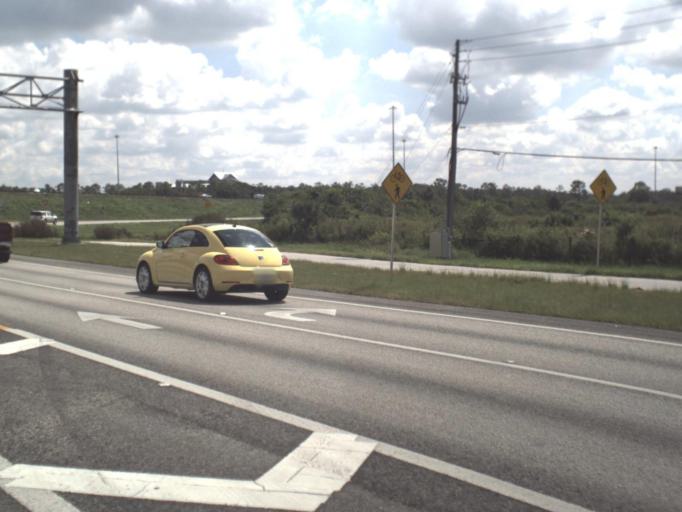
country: US
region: Florida
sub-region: Lee County
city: Fort Myers
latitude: 26.6127
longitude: -81.8058
